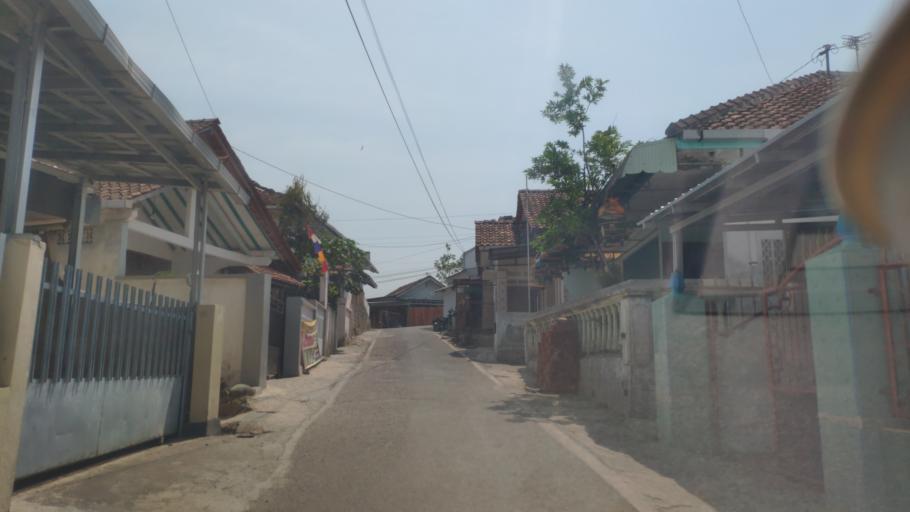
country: ID
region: Central Java
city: Wonosobo
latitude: -7.3982
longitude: 109.7005
